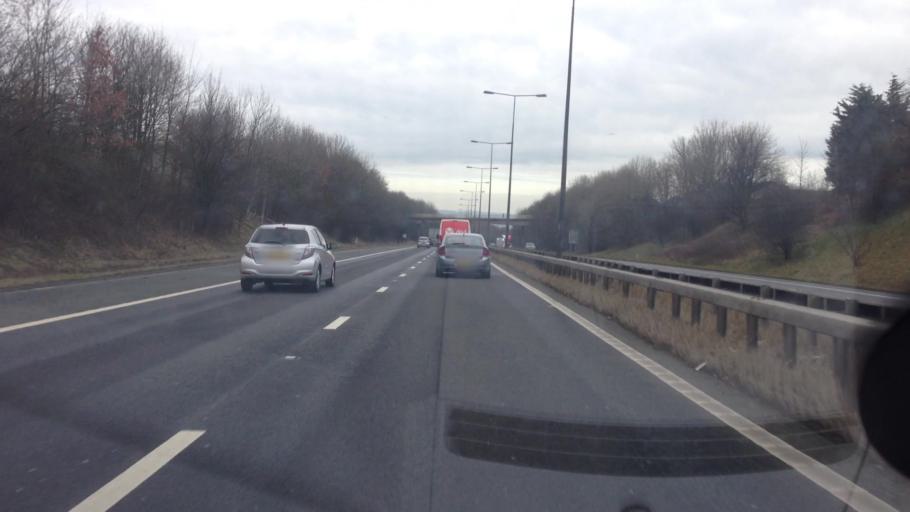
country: GB
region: England
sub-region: City and Borough of Leeds
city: Gildersome
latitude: 53.7516
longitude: -1.6170
